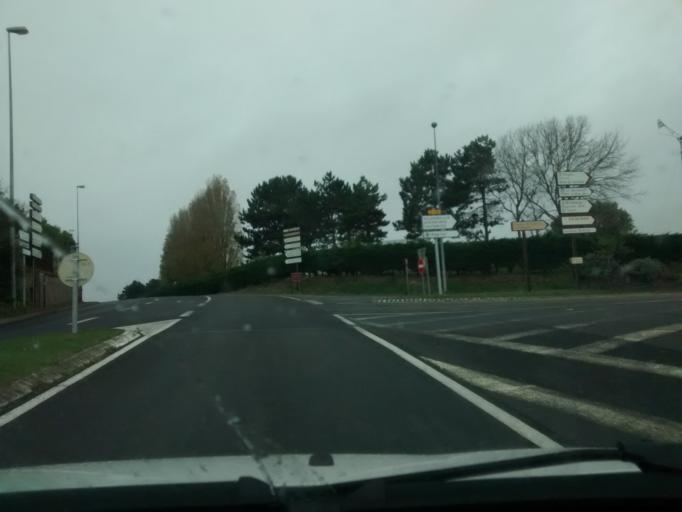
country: FR
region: Lower Normandy
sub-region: Departement de la Manche
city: Saint-Pair-sur-Mer
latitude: 48.8275
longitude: -1.5789
